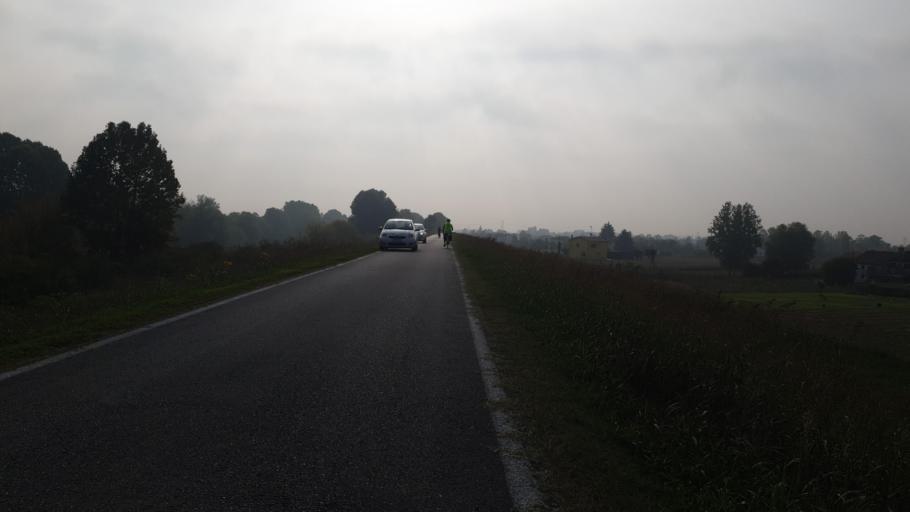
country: IT
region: Veneto
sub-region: Provincia di Venezia
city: Galta
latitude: 45.3796
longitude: 12.0209
